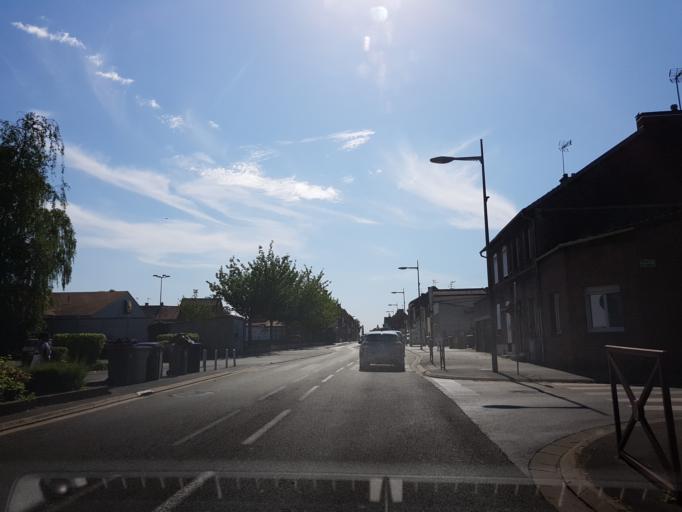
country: FR
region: Nord-Pas-de-Calais
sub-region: Departement du Nord
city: Lourches
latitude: 50.3128
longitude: 3.3468
